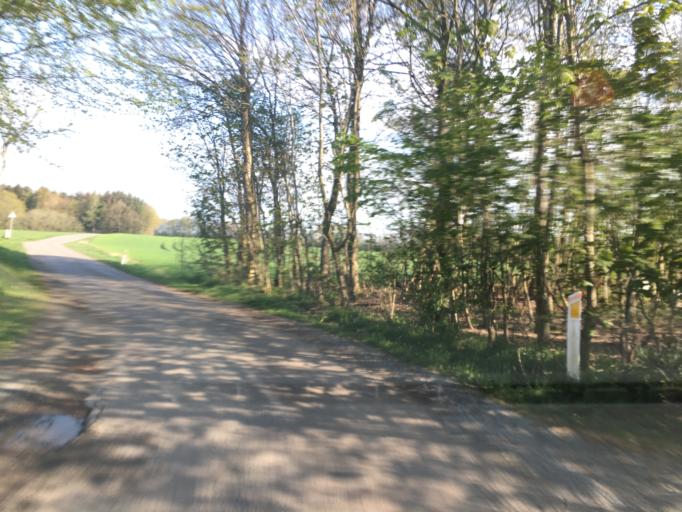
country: DK
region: South Denmark
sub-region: Aabenraa Kommune
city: Rodekro
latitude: 55.1348
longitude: 9.3814
